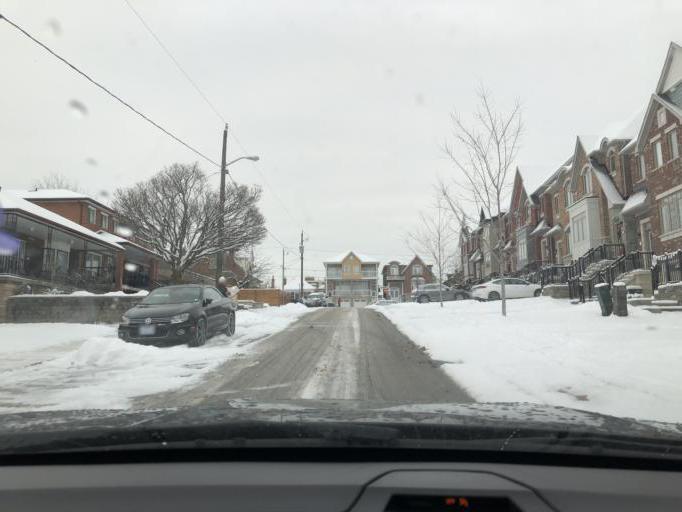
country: CA
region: Ontario
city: Toronto
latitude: 43.6884
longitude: -79.4705
